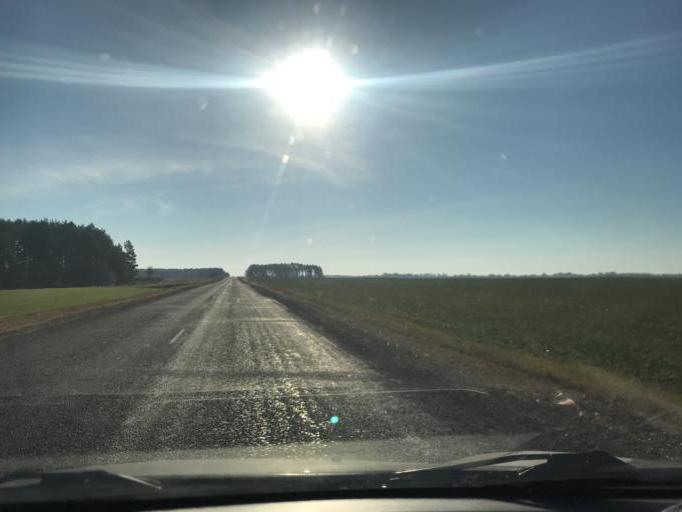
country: BY
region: Gomel
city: Khoyniki
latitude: 51.8188
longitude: 30.0854
